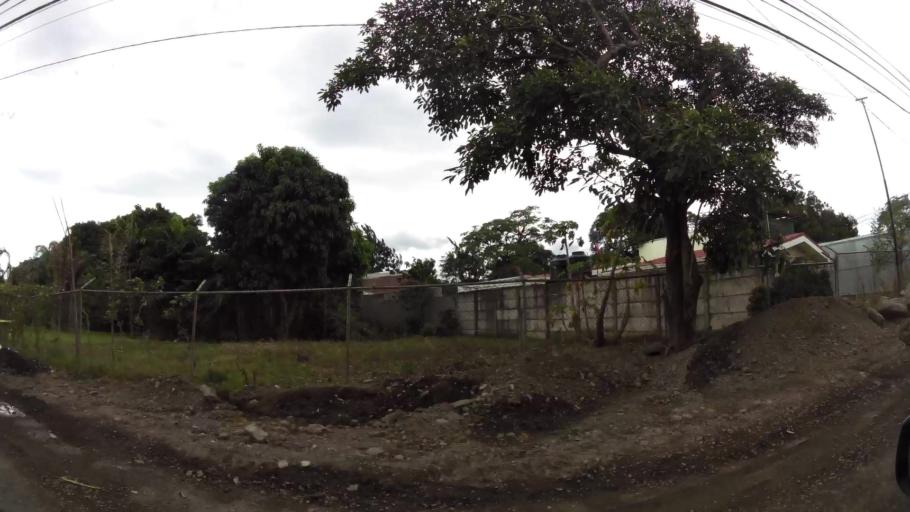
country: CR
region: Heredia
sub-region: Canton de Belen
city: San Antonio
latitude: 9.9613
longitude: -84.1943
